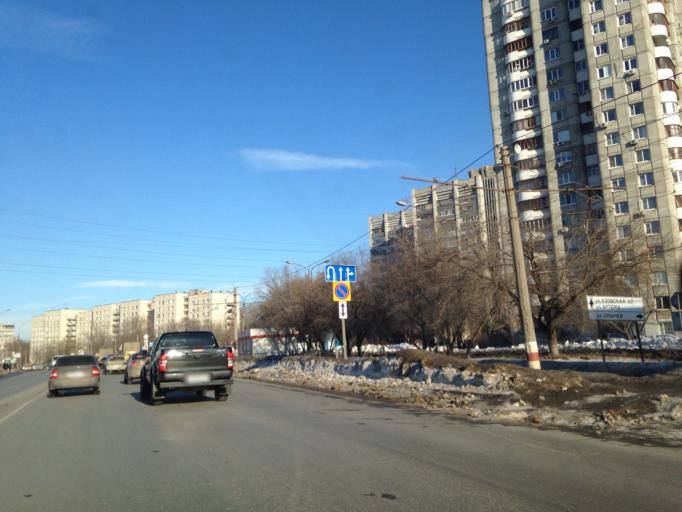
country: RU
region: Ulyanovsk
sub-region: Ulyanovskiy Rayon
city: Ulyanovsk
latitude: 54.3143
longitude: 48.3549
